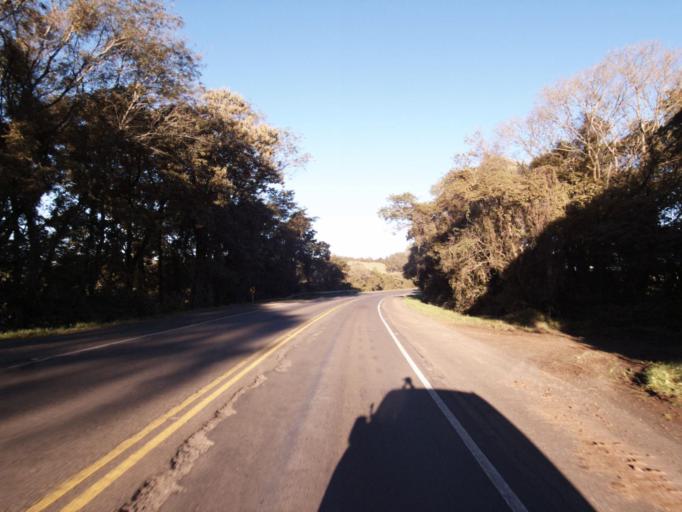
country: BR
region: Santa Catarina
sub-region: Sao Lourenco Do Oeste
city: Sao Lourenco dOeste
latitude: -26.7740
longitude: -53.2714
